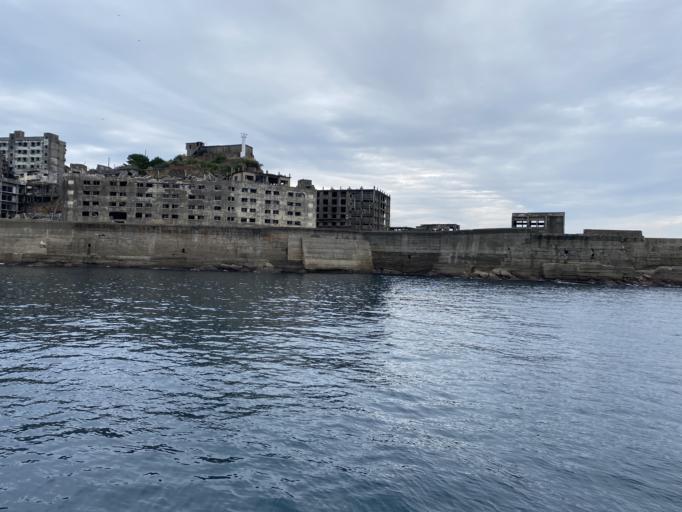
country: JP
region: Nagasaki
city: Nagasaki-shi
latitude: 32.6274
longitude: 129.7356
